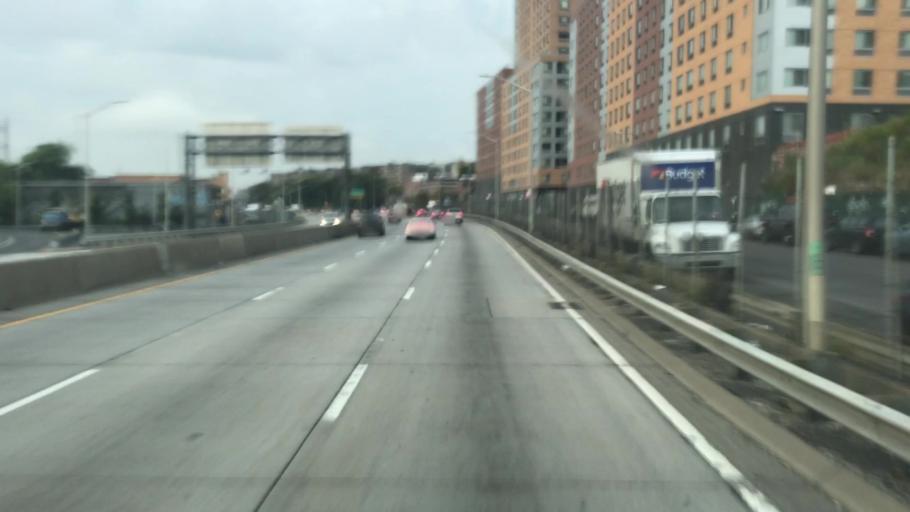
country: US
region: New York
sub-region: Bronx
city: The Bronx
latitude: 40.8334
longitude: -73.8837
